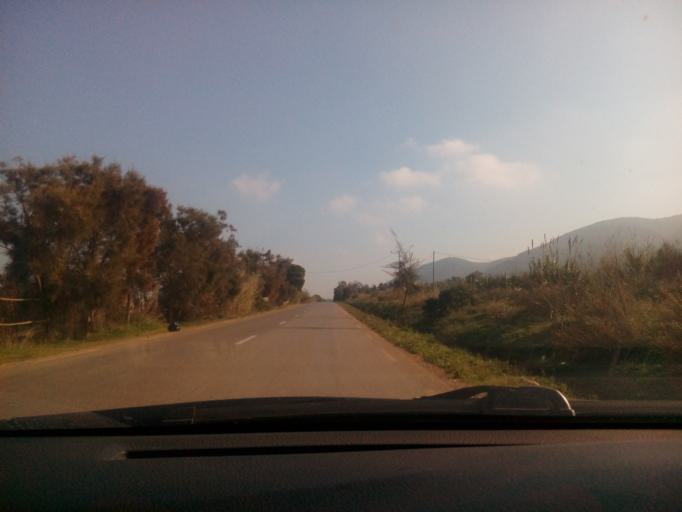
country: DZ
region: Oran
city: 'Ain el Turk
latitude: 35.7022
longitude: -0.8572
